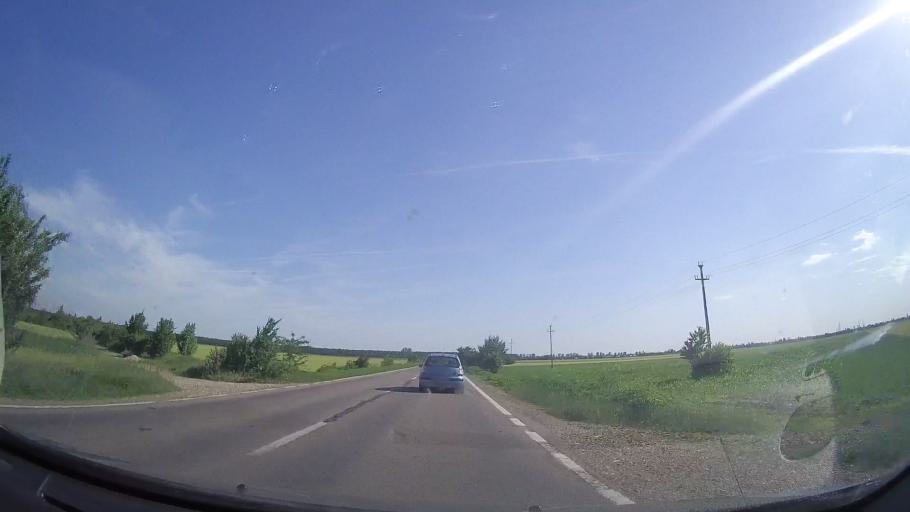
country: RO
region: Prahova
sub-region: Comuna Berceni
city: Berceni
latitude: 44.9263
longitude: 26.1029
